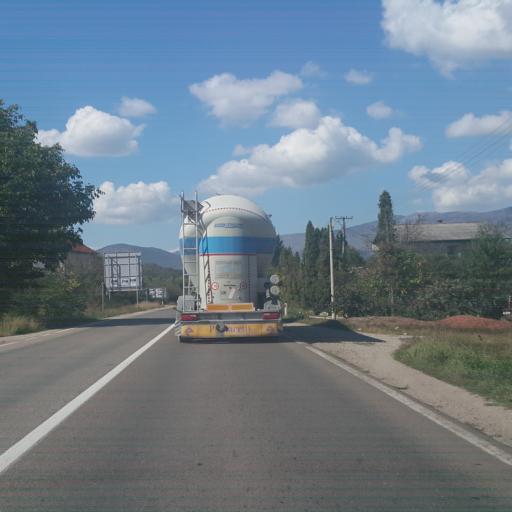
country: RS
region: Central Serbia
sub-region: Pirotski Okrug
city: Bela Palanka
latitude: 43.2737
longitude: 22.2326
